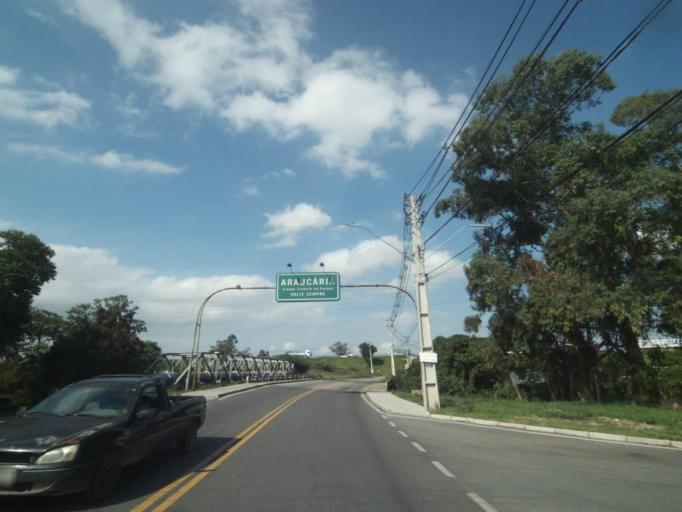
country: BR
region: Parana
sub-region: Araucaria
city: Araucaria
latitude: -25.5151
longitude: -49.3388
